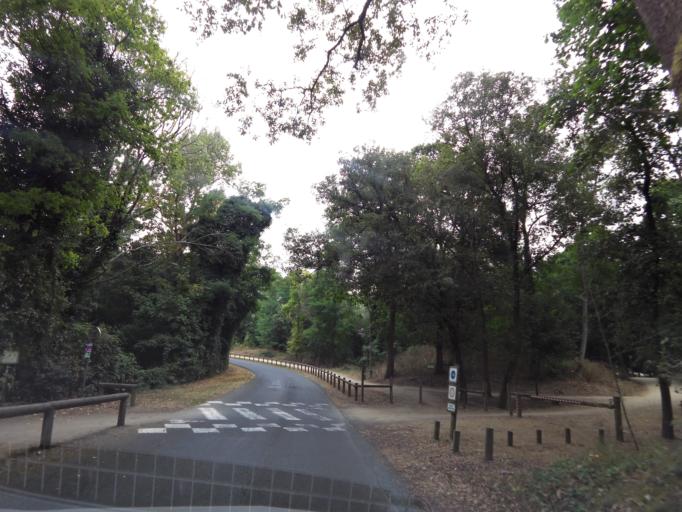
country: FR
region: Pays de la Loire
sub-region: Departement de la Vendee
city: Longeville-sur-Mer
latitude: 46.4074
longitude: -1.4935
